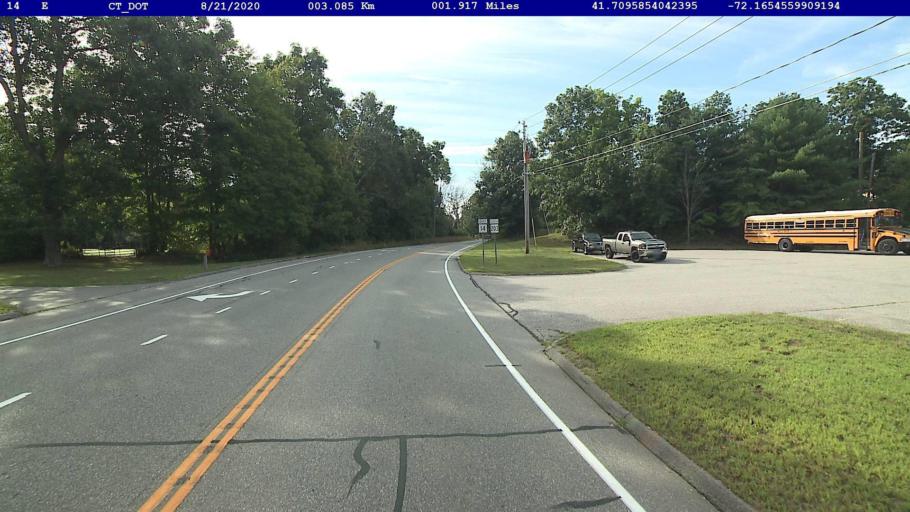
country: US
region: Connecticut
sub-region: Windham County
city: Windham
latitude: 41.7096
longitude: -72.1655
